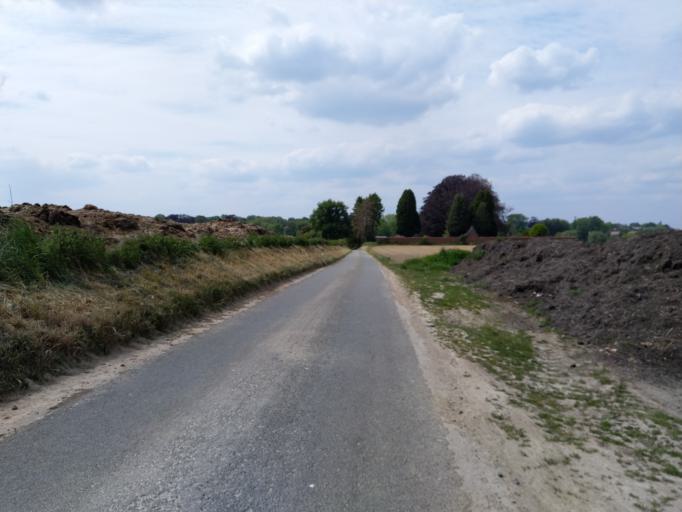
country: BE
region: Wallonia
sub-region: Province du Hainaut
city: Silly
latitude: 50.5957
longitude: 3.9468
